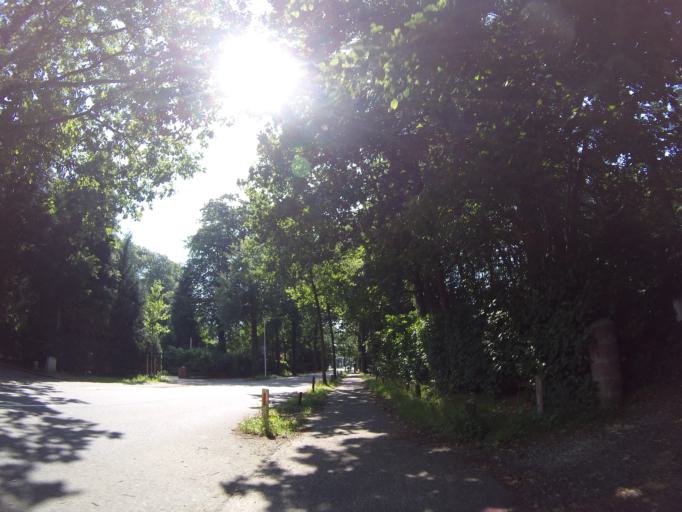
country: NL
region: Utrecht
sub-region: Gemeente Zeist
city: Zeist
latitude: 52.1095
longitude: 5.2373
